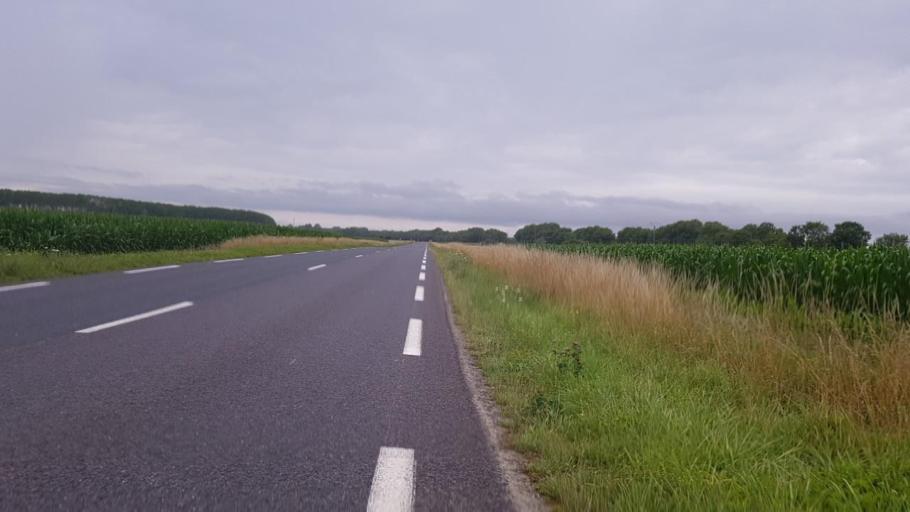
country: FR
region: Champagne-Ardenne
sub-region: Departement de la Marne
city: Pargny-sur-Saulx
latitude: 48.7557
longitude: 4.7228
